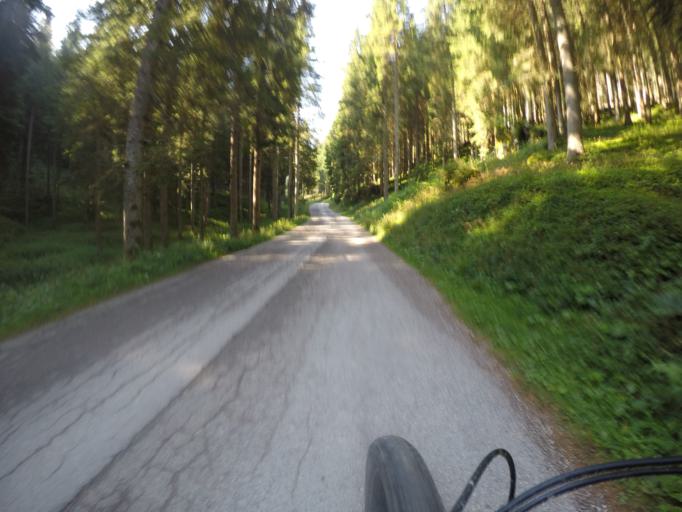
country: IT
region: Veneto
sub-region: Provincia di Vicenza
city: Asiago
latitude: 45.8392
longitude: 11.5219
